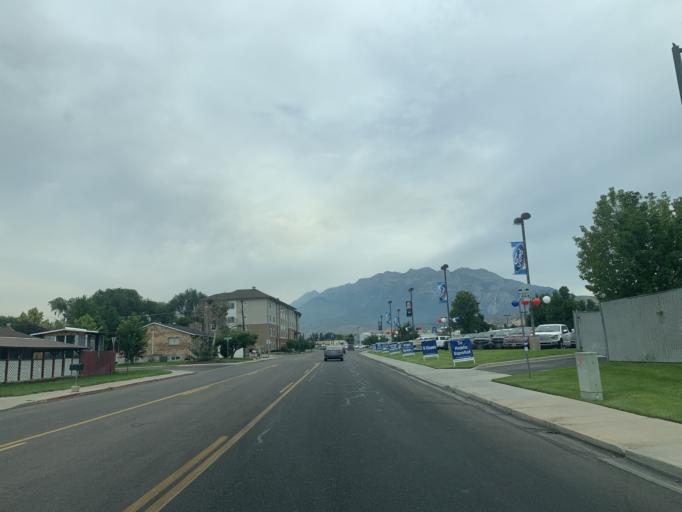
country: US
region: Utah
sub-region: Utah County
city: Provo
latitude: 40.2589
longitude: -111.6679
